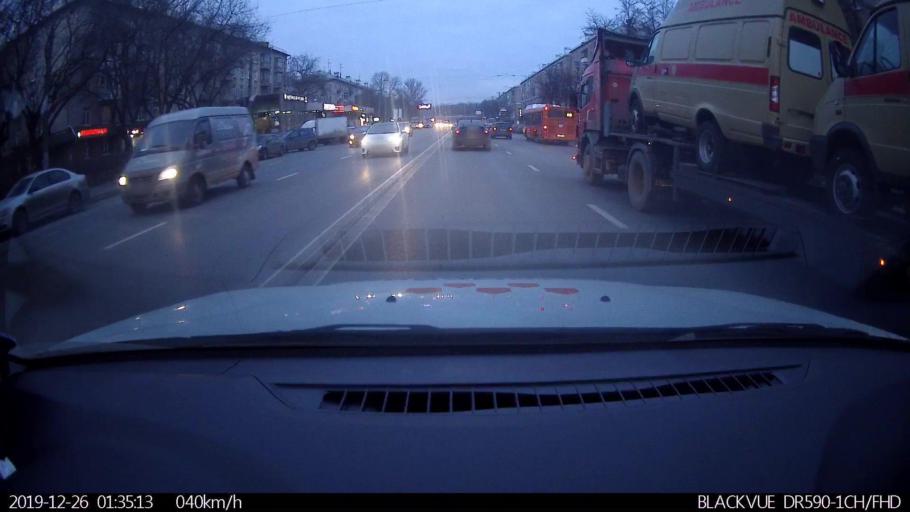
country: RU
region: Nizjnij Novgorod
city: Nizhniy Novgorod
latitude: 56.2648
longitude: 43.9116
